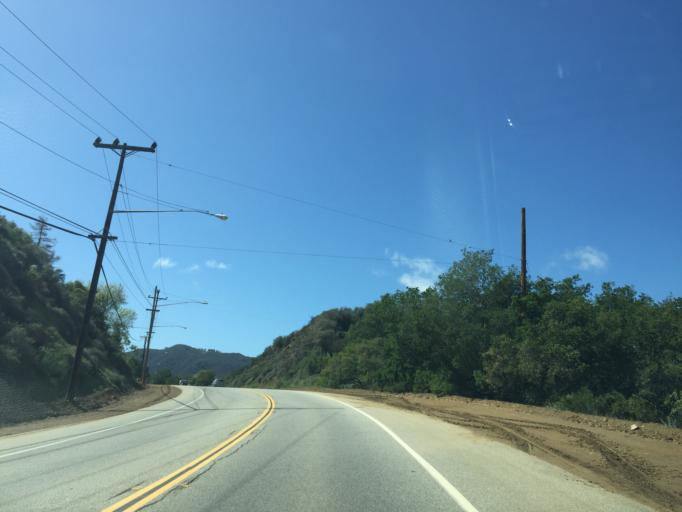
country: US
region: California
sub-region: Los Angeles County
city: Westlake Village
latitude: 34.0956
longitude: -118.8142
